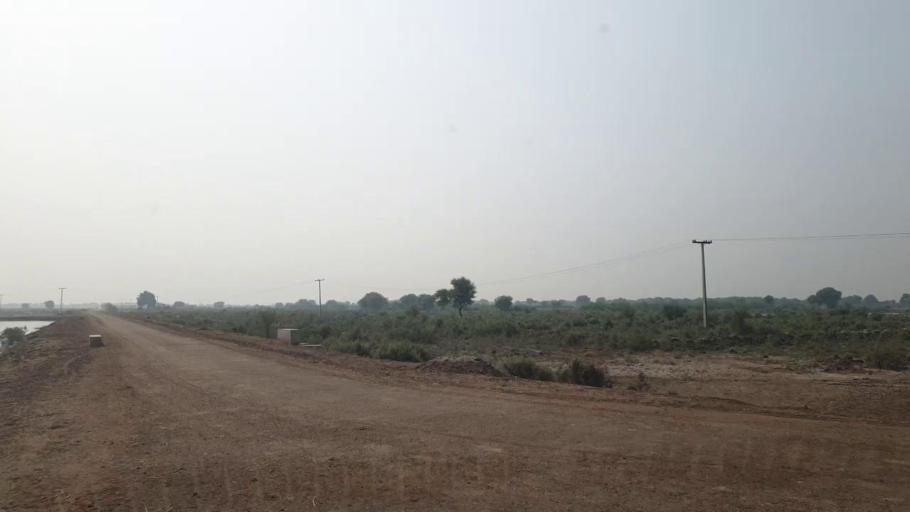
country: PK
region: Sindh
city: Matli
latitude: 25.1414
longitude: 68.6907
